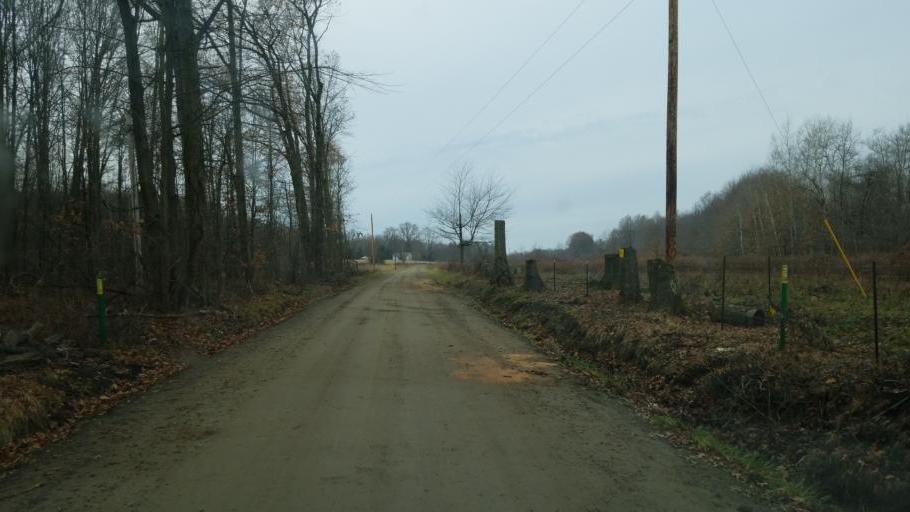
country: US
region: Pennsylvania
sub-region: Crawford County
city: Cochranton
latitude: 41.5057
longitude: -80.1329
